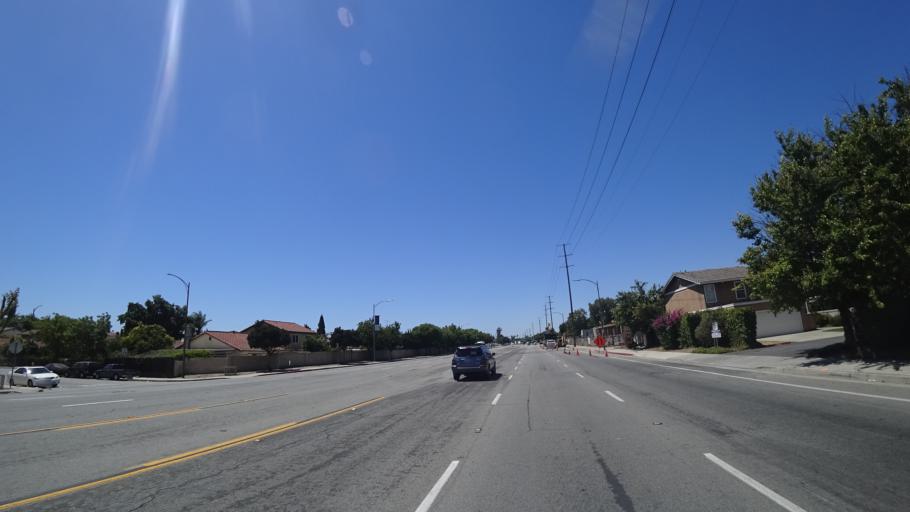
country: US
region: California
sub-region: Santa Clara County
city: Seven Trees
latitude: 37.3059
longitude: -121.8456
